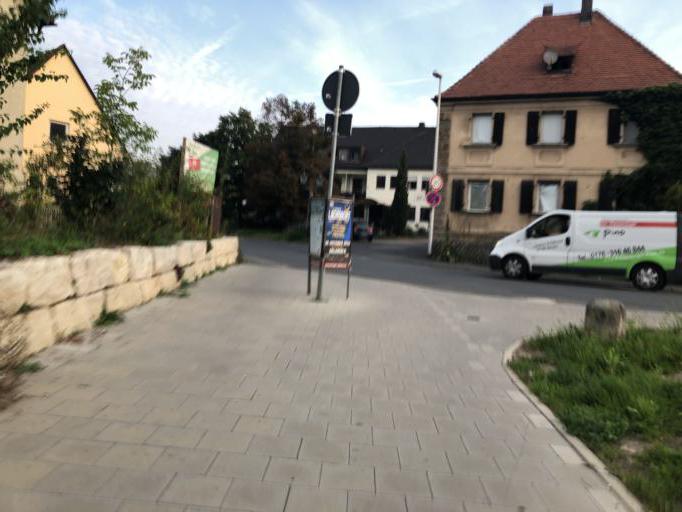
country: DE
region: Bavaria
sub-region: Regierungsbezirk Mittelfranken
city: Erlangen
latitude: 49.5890
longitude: 10.9600
